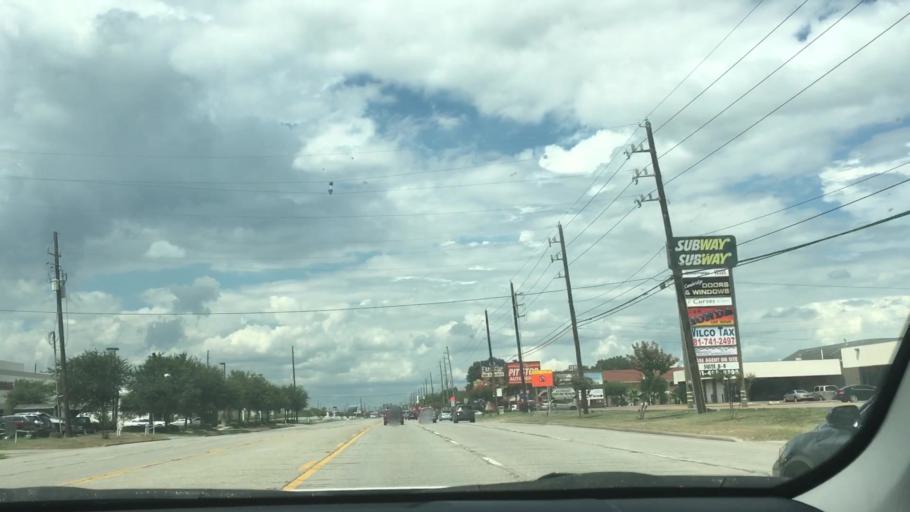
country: US
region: Texas
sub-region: Fort Bend County
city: Stafford
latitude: 29.6348
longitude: -95.5650
